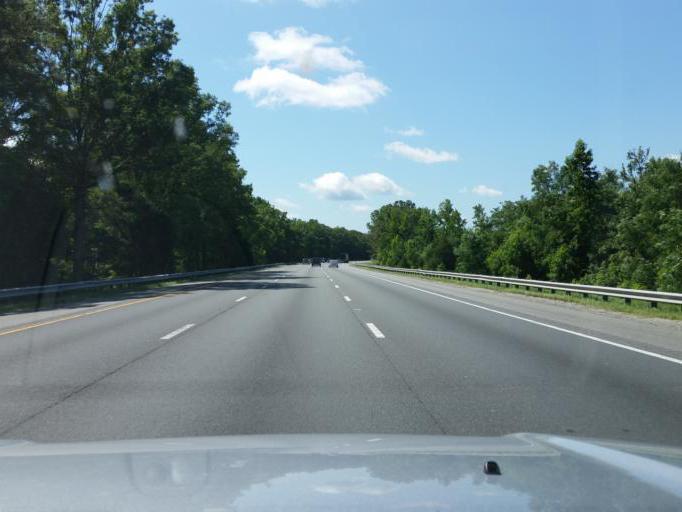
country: US
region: Virginia
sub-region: Spotsylvania County
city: Spotsylvania Courthouse
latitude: 38.2157
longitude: -77.4991
